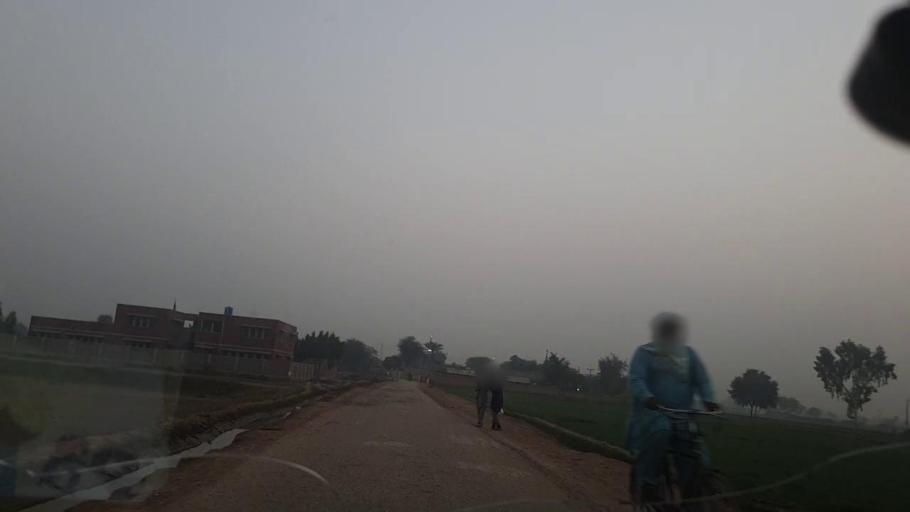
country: PK
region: Sindh
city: Hingorja
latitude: 27.2222
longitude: 68.4277
